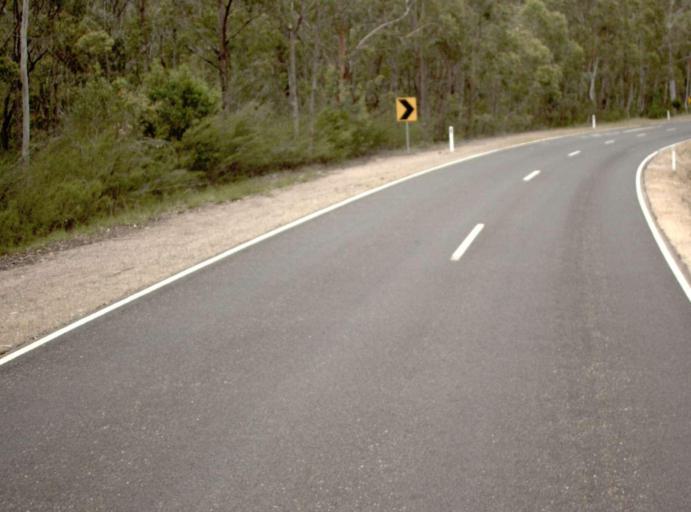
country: AU
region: Victoria
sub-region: East Gippsland
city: Bairnsdale
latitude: -37.6358
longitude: 147.2431
